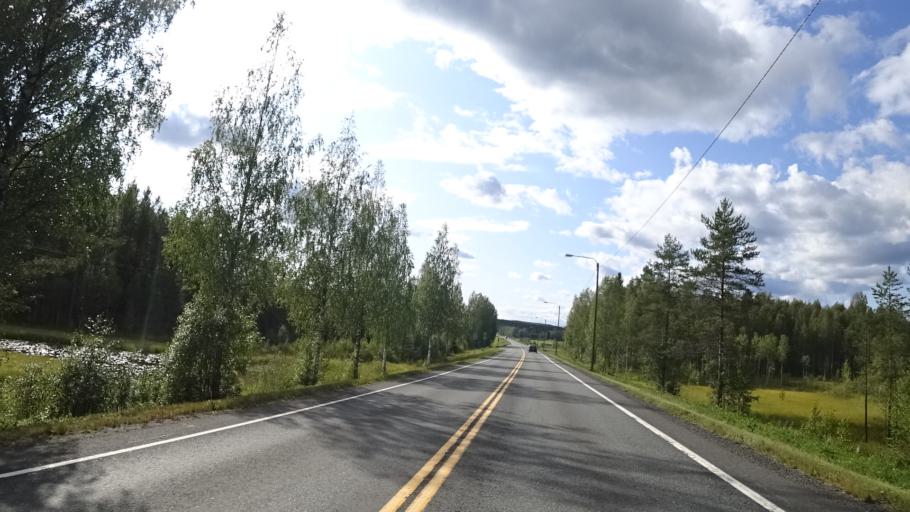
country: FI
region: North Karelia
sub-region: Keski-Karjala
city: Tohmajaervi
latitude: 62.2204
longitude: 30.3995
